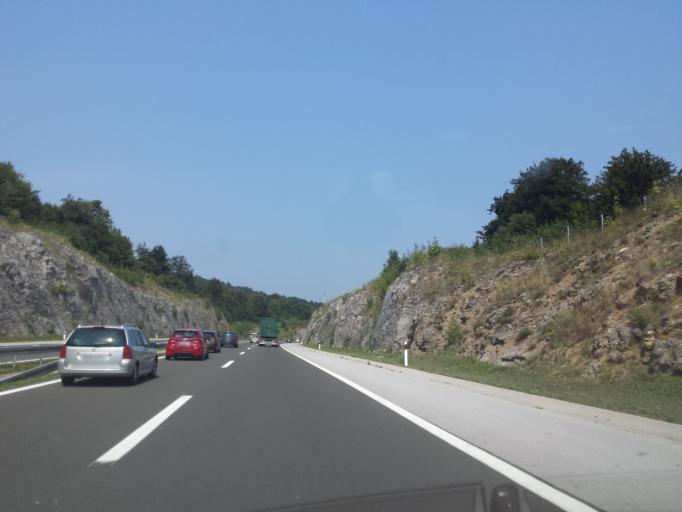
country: HR
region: Karlovacka
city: Ostarije
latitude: 45.2627
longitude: 15.2729
